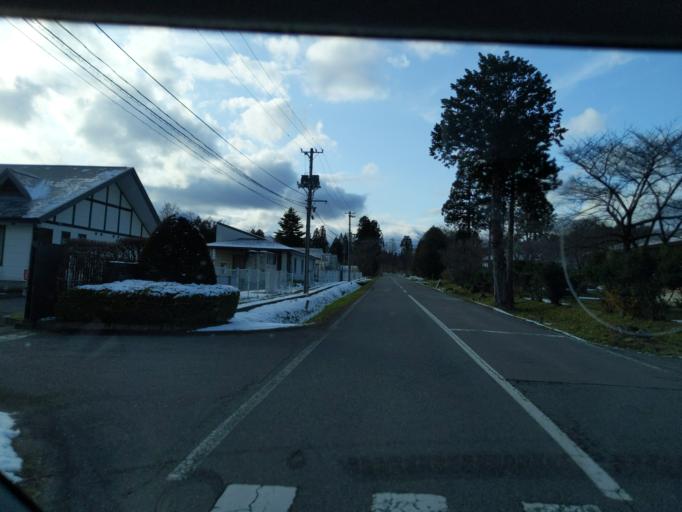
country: JP
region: Iwate
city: Kitakami
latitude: 39.2351
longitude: 141.0439
